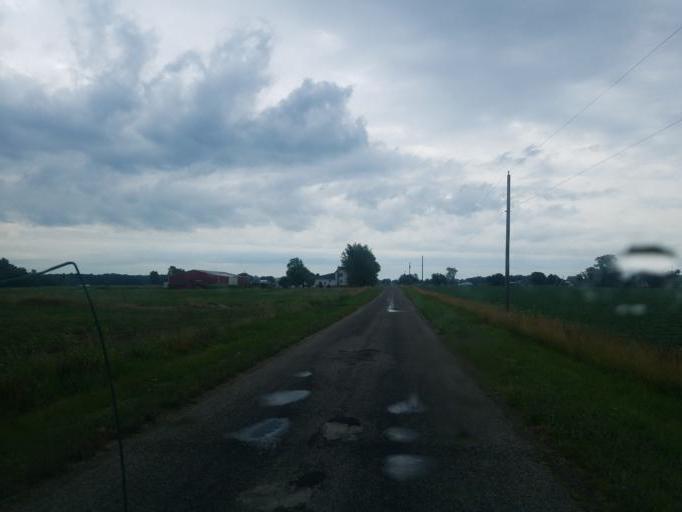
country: US
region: Ohio
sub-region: Defiance County
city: Hicksville
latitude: 41.3681
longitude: -84.7929
